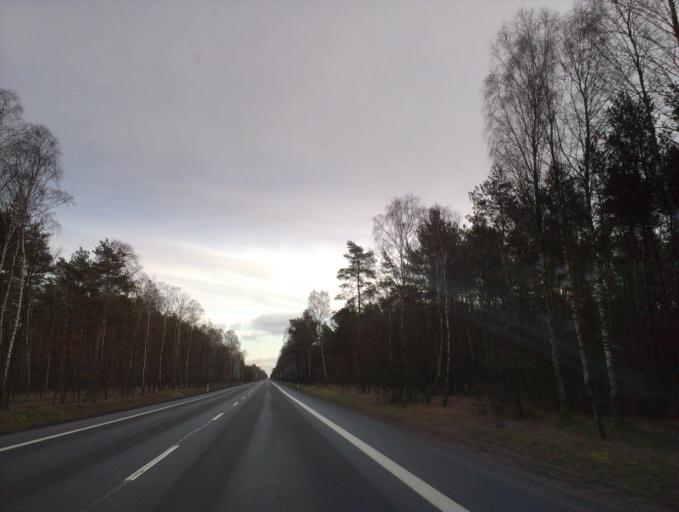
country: PL
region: Masovian Voivodeship
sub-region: Powiat sierpecki
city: Szczutowo
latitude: 52.8877
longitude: 19.5748
